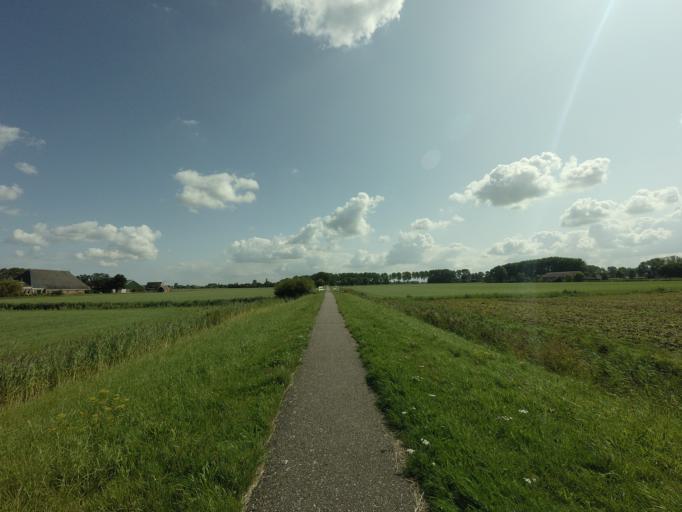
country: NL
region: Friesland
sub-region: Gemeente Leeuwarderadeel
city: Stiens
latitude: 53.2827
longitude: 5.7137
